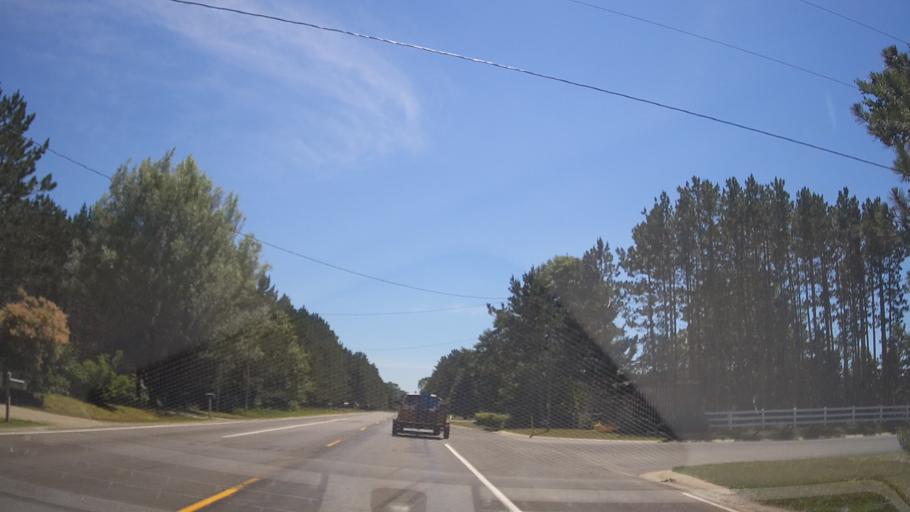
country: US
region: Michigan
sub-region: Grand Traverse County
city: Traverse City
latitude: 44.6472
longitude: -85.6965
